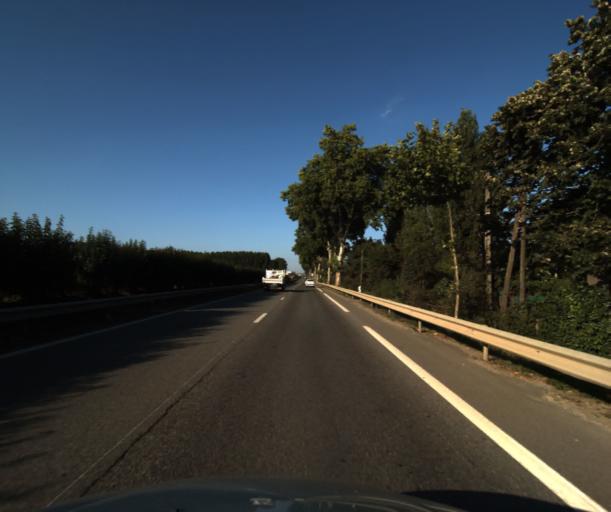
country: FR
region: Midi-Pyrenees
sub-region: Departement de la Haute-Garonne
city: Roquettes
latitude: 43.5025
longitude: 1.3568
